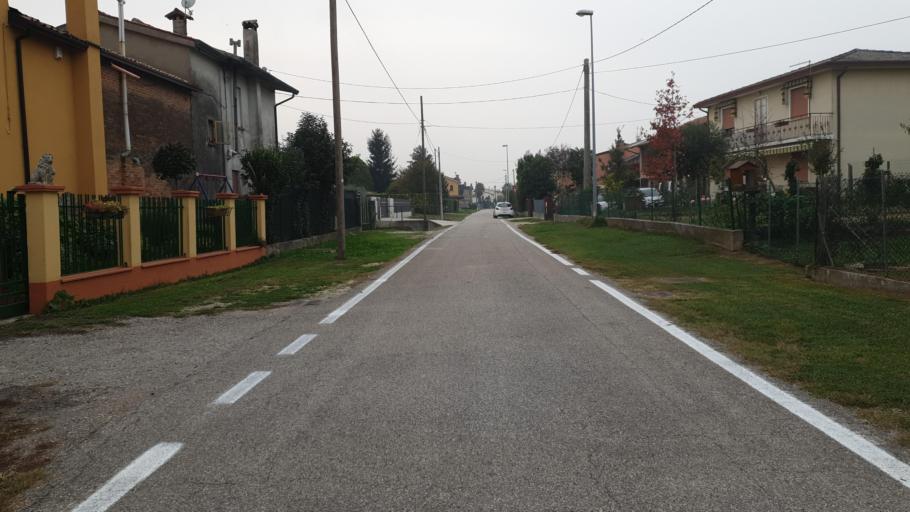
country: IT
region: Veneto
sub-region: Provincia di Padova
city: Bertipaglia
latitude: 45.3198
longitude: 11.8932
